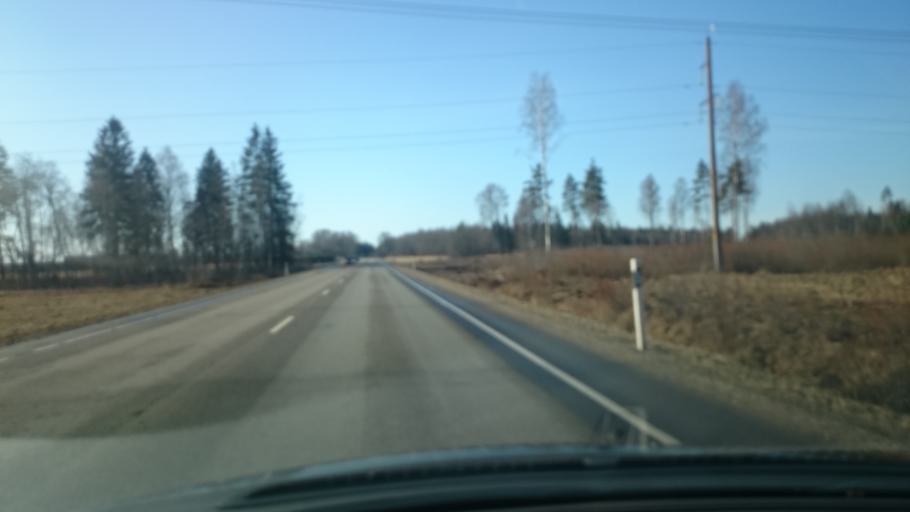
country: EE
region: Harju
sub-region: Saku vald
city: Saku
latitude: 59.2623
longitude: 24.7409
